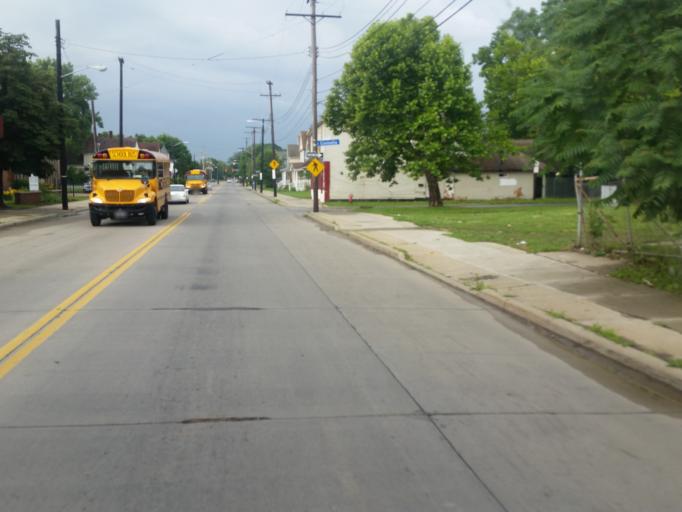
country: US
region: Ohio
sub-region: Cuyahoga County
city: Bratenahl
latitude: 41.5227
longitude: -81.6337
